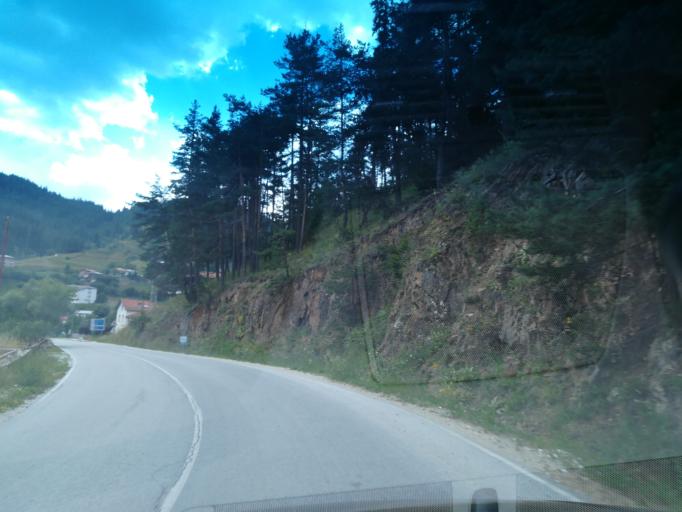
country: BG
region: Smolyan
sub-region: Obshtina Chepelare
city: Chepelare
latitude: 41.6630
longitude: 24.6389
